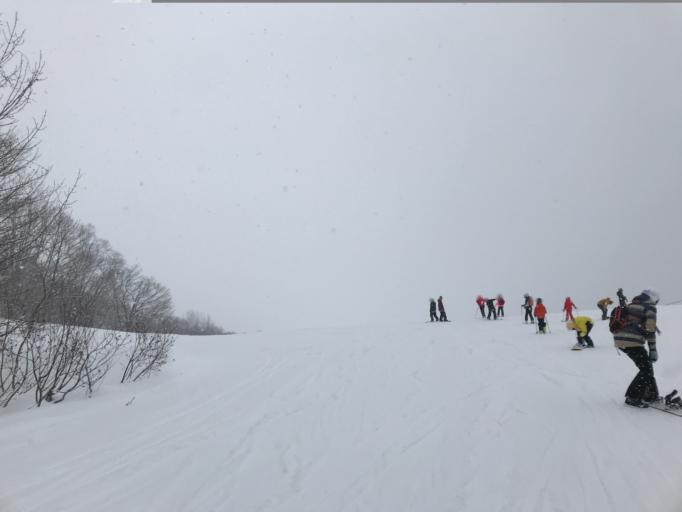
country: JP
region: Nagano
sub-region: Kitaazumi Gun
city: Hakuba
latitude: 36.7524
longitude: 137.8495
